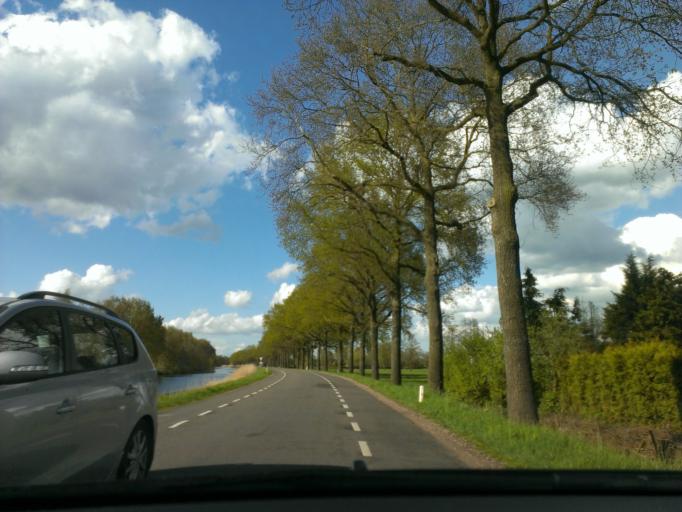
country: NL
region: Gelderland
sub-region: Gemeente Epe
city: Oene
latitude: 52.3458
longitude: 6.0242
